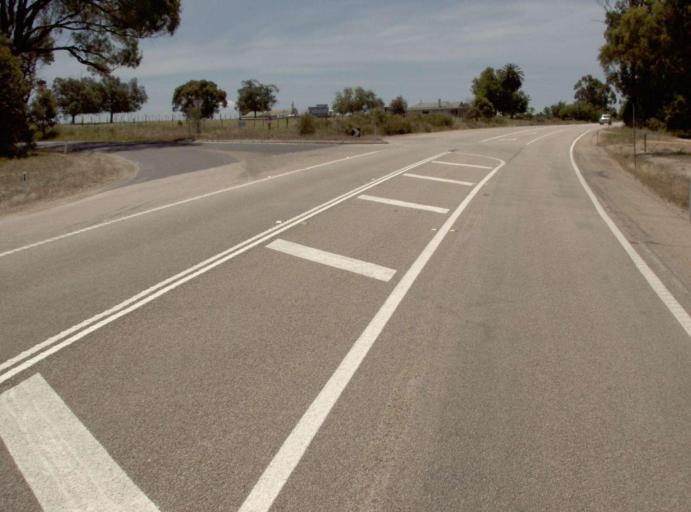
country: AU
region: Victoria
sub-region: East Gippsland
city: Bairnsdale
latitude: -37.7794
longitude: 147.6839
